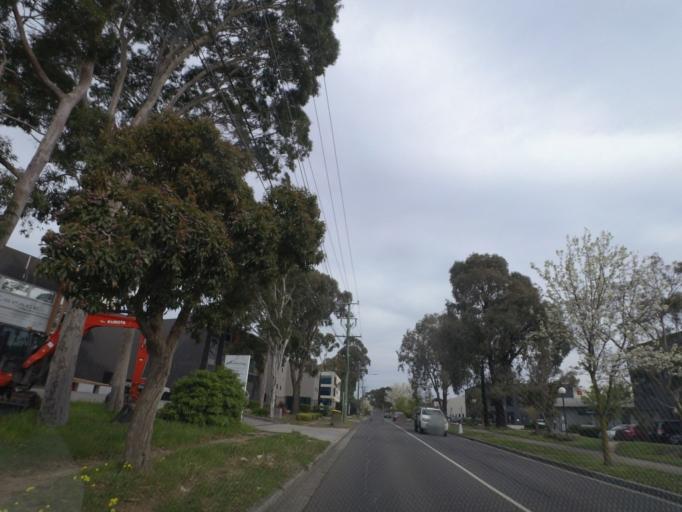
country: AU
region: Victoria
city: Forest Hill
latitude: -37.8317
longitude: 145.1874
